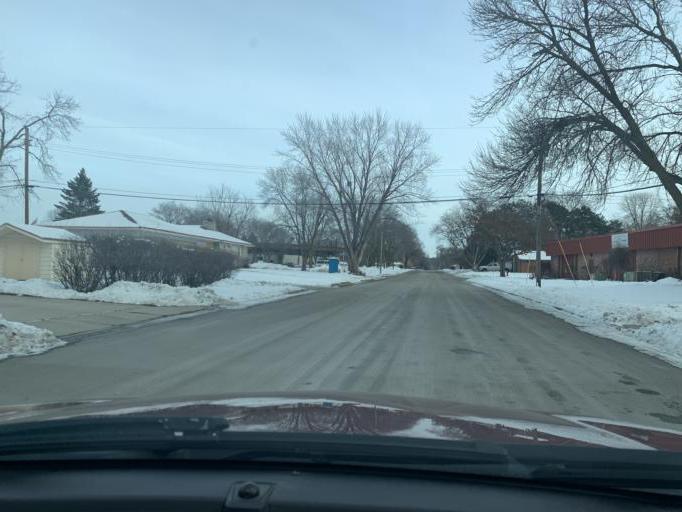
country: US
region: Minnesota
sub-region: Washington County
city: Saint Paul Park
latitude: 44.8404
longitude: -92.9896
